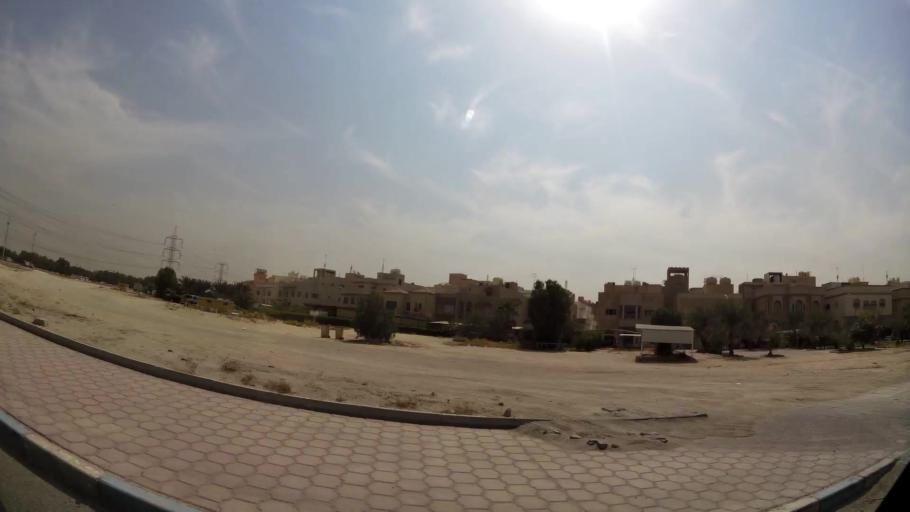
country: KW
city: Bayan
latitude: 29.2894
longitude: 48.0268
